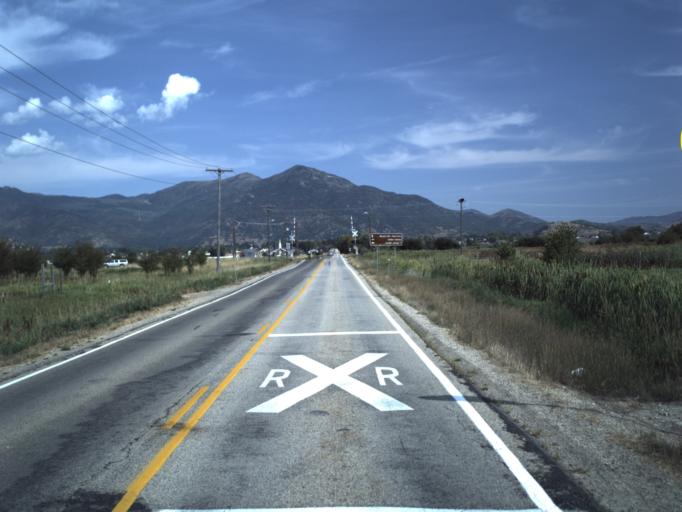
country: US
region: Utah
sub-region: Wasatch County
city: Midway
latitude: 40.4849
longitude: -111.4719
